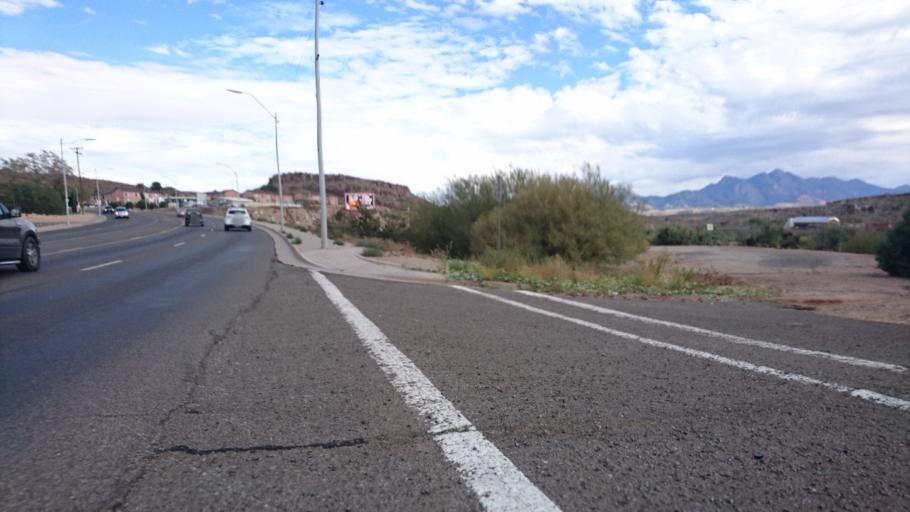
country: US
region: Arizona
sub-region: Mohave County
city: Kingman
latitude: 35.1864
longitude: -114.0420
